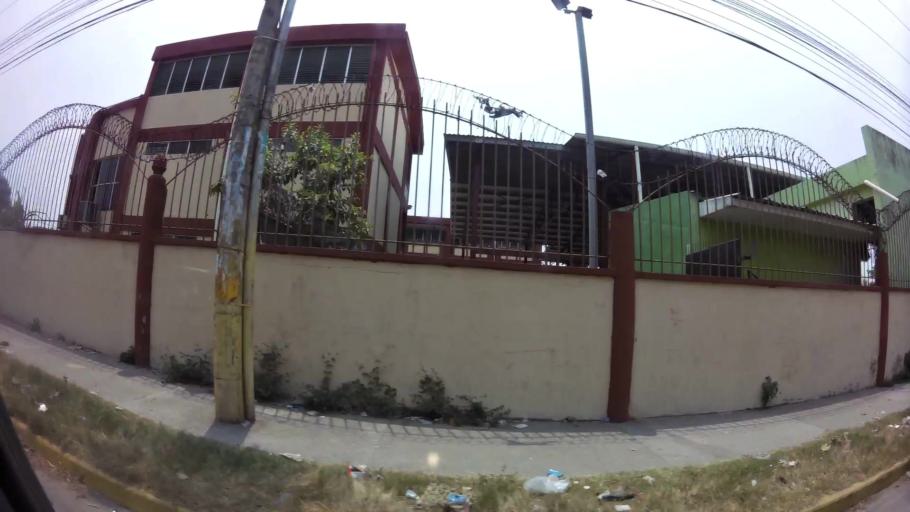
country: HN
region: Cortes
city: San Pedro Sula
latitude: 15.4913
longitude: -88.0116
